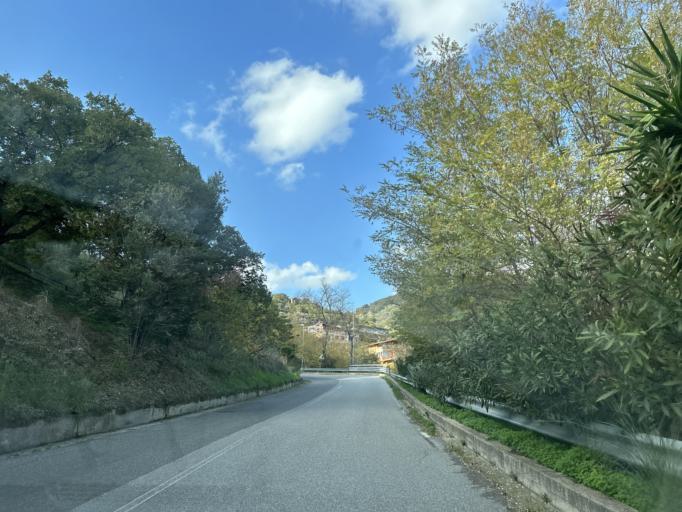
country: IT
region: Calabria
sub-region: Provincia di Catanzaro
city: Montepaone
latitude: 38.7228
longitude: 16.5071
